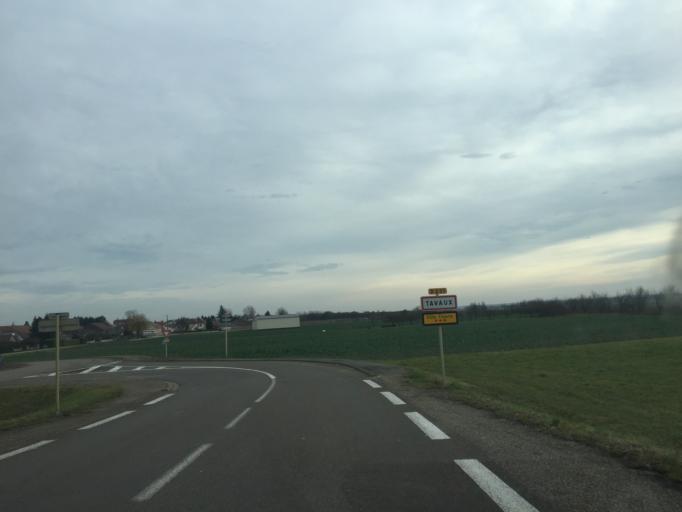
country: FR
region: Franche-Comte
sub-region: Departement du Jura
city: Tavaux
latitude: 47.0327
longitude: 5.4078
